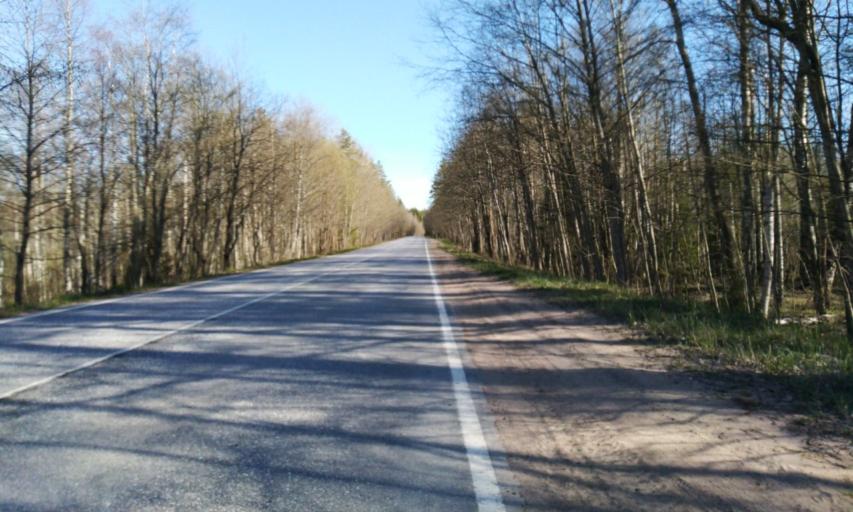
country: RU
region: Leningrad
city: Garbolovo
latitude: 60.3514
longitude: 30.4436
